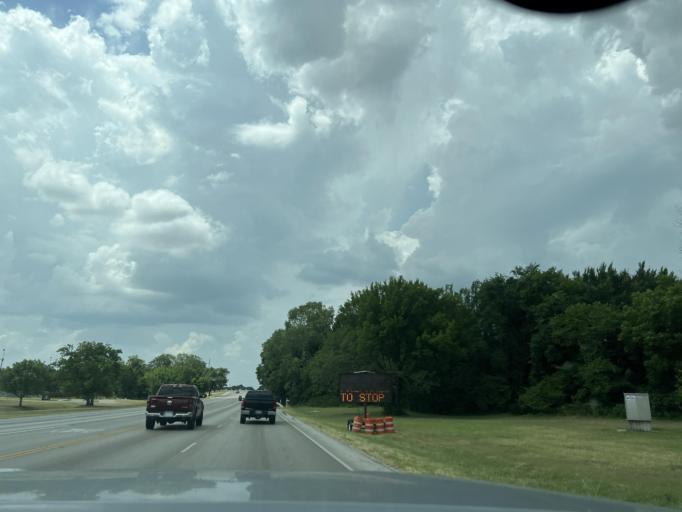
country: US
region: Texas
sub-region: Wise County
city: Decatur
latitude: 33.2120
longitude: -97.5991
